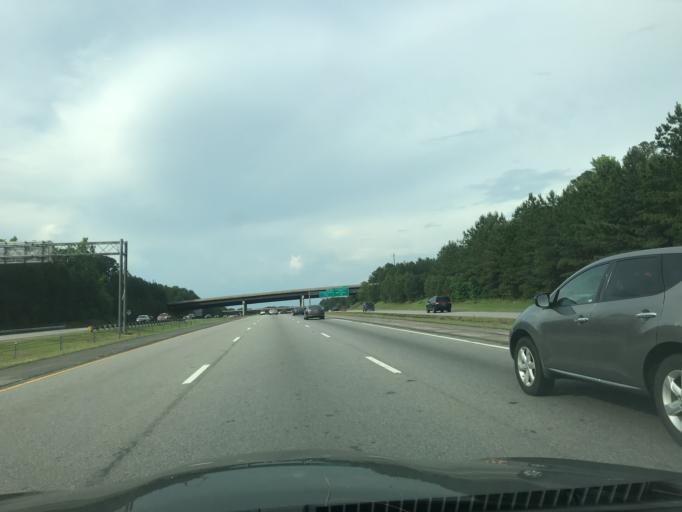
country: US
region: North Carolina
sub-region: Wake County
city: Morrisville
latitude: 35.8850
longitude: -78.8203
